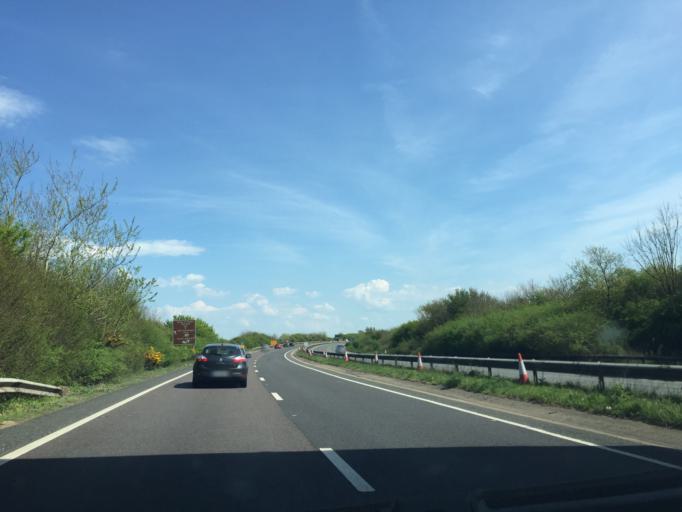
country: GB
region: England
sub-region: Kent
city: Folkestone
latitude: 51.1105
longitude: 1.2273
